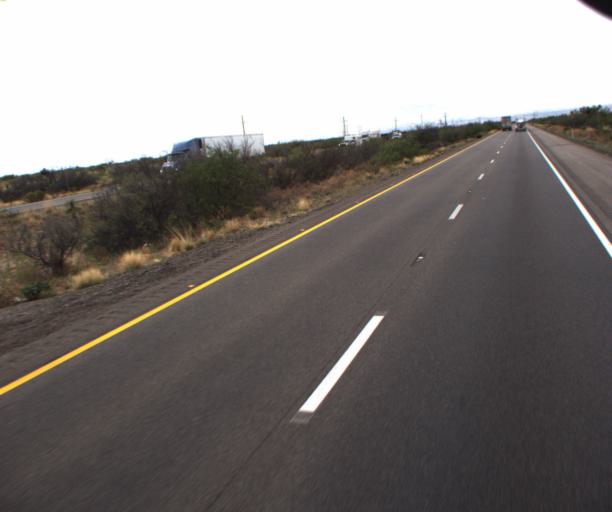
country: US
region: Arizona
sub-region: Cochise County
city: Saint David
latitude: 32.0042
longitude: -110.1454
